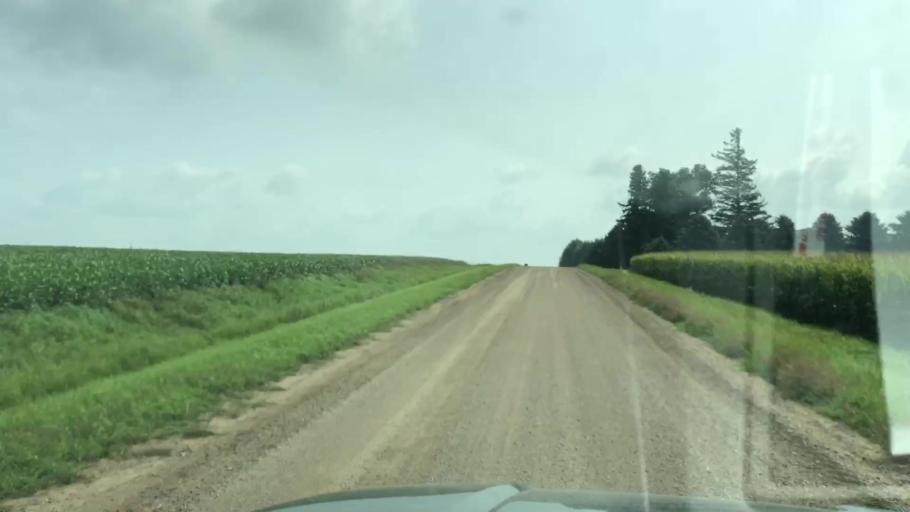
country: US
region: Iowa
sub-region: O'Brien County
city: Sheldon
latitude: 43.2154
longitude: -95.9391
